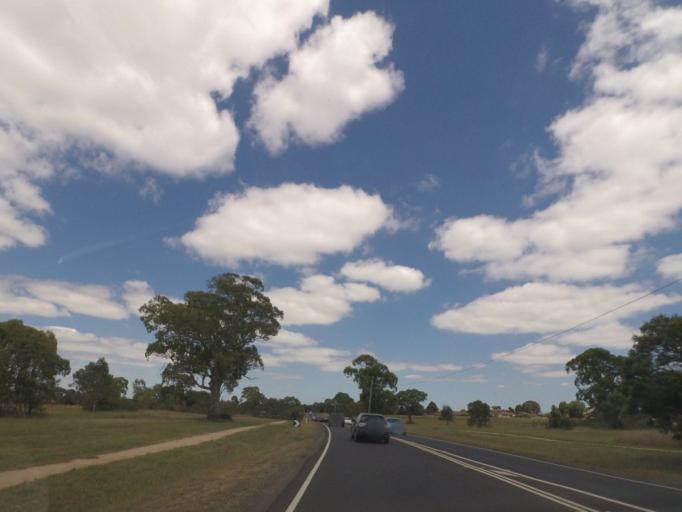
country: AU
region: Victoria
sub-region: Whittlesea
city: Epping
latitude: -37.6622
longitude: 145.0432
